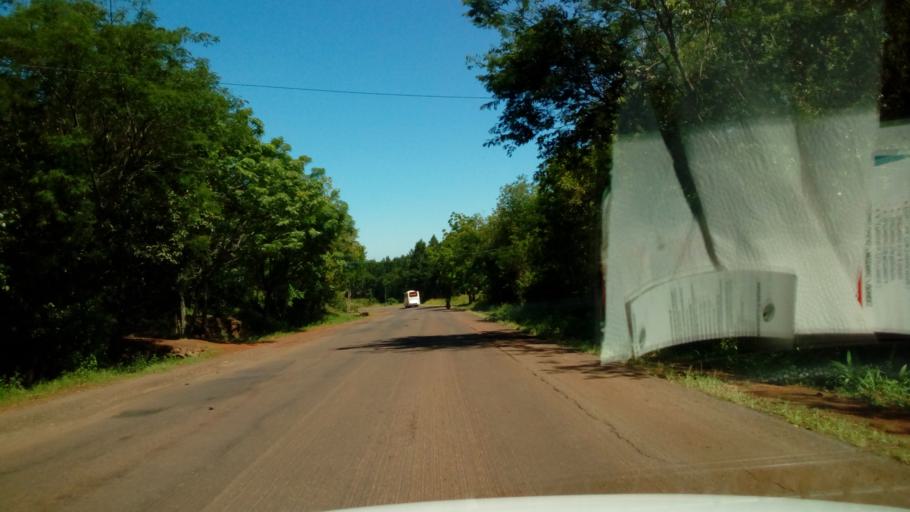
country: AR
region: Misiones
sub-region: Departamento de Leandro N. Alem
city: Leandro N. Alem
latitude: -27.5908
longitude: -55.3586
